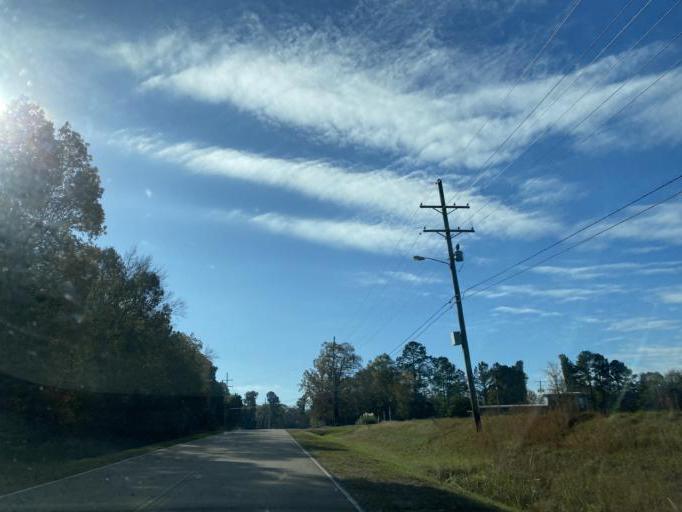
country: US
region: Mississippi
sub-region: Madison County
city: Ridgeland
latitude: 32.4724
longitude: -90.1792
